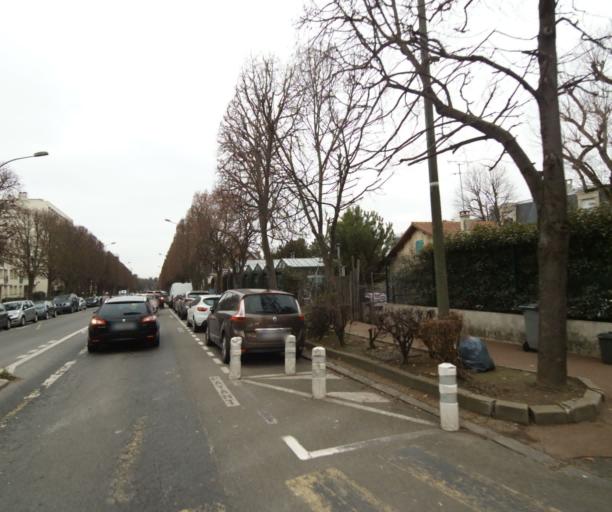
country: FR
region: Ile-de-France
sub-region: Departement des Hauts-de-Seine
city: Saint-Cloud
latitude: 48.8543
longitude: 2.2121
